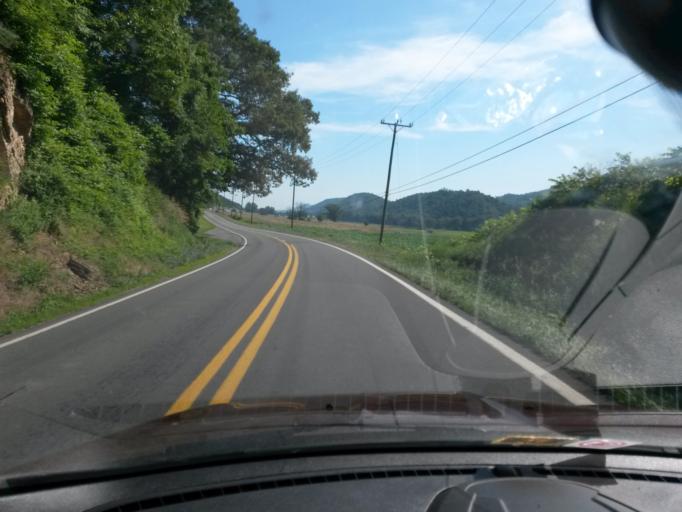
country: US
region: Virginia
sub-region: Shenandoah County
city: Basye
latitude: 38.9863
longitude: -78.7833
